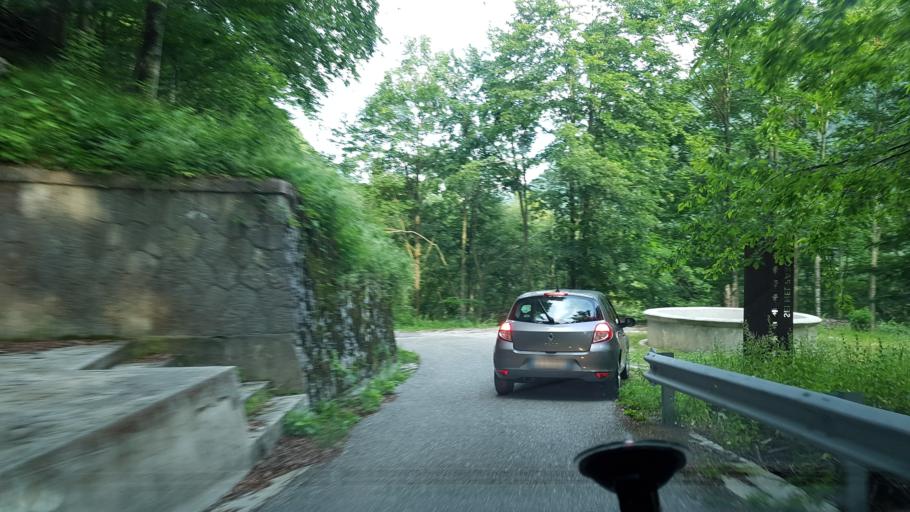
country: IT
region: Friuli Venezia Giulia
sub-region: Provincia di Udine
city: Prato
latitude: 46.3277
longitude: 13.3685
